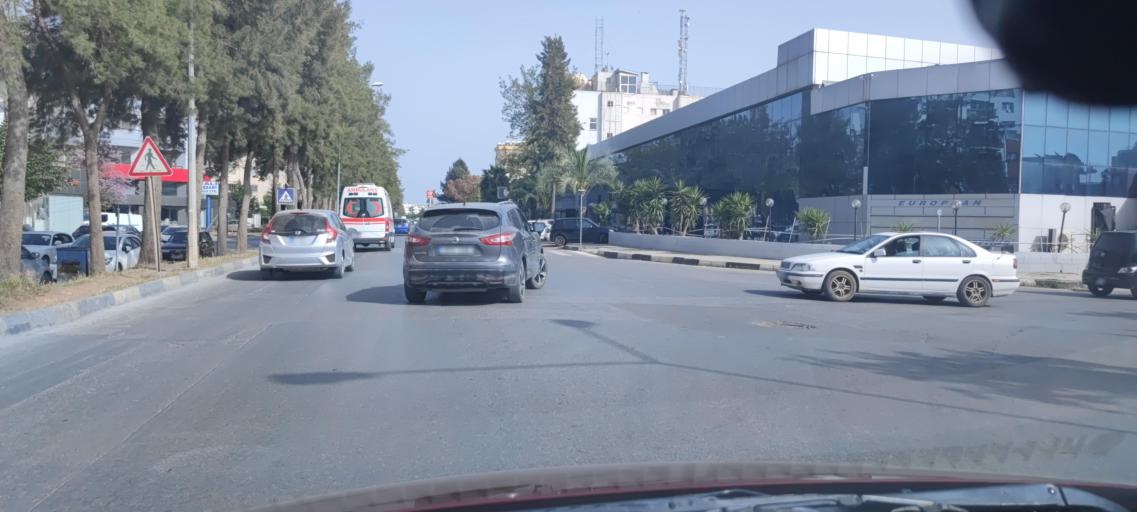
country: CY
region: Ammochostos
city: Famagusta
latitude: 35.1250
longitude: 33.9277
